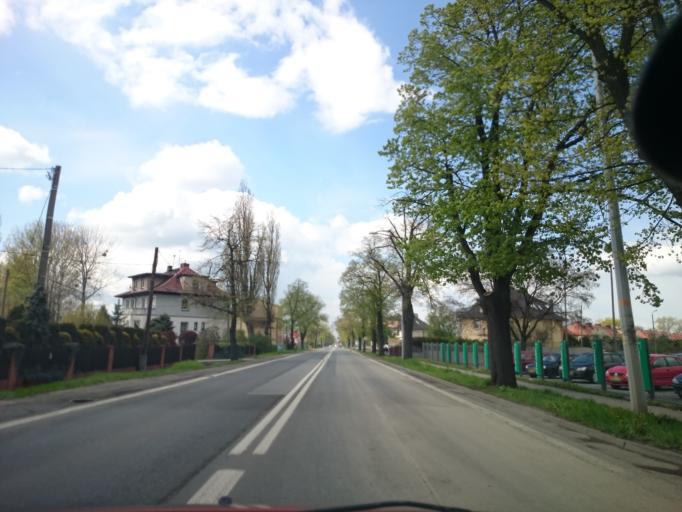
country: PL
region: Opole Voivodeship
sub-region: Powiat opolski
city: Opole
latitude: 50.6536
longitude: 17.9594
